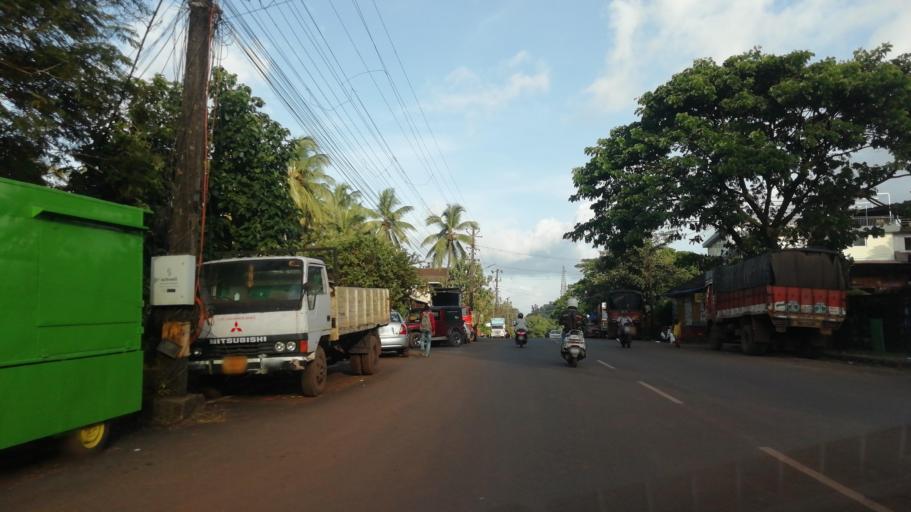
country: IN
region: Goa
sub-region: North Goa
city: Ponda
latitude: 15.4001
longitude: 74.0157
